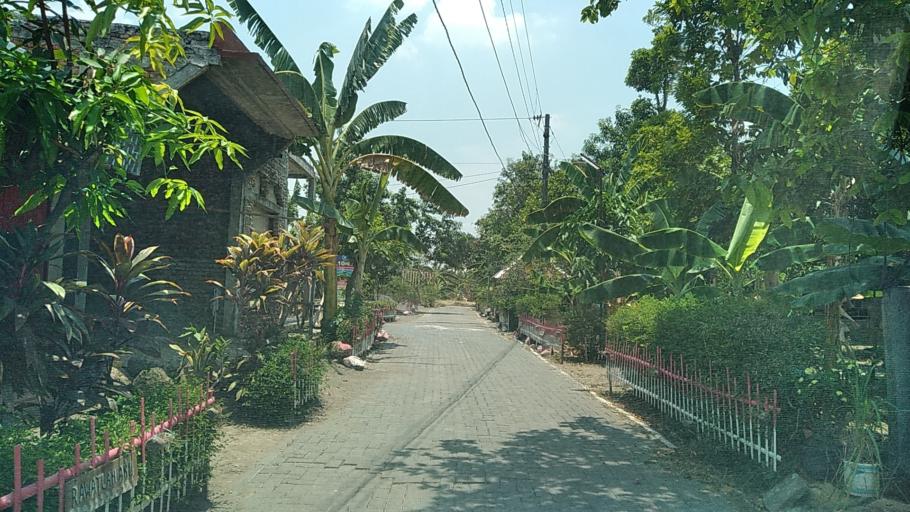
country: ID
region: Central Java
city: Mranggen
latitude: -7.0089
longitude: 110.4909
